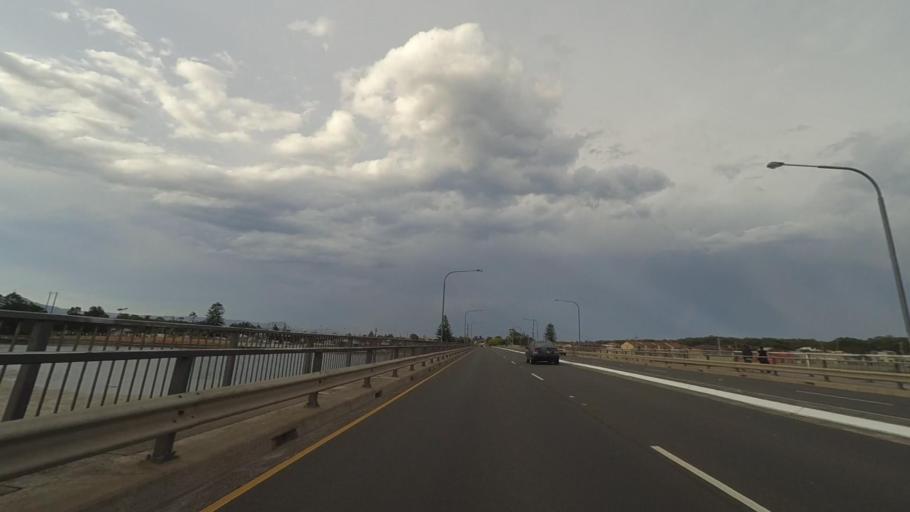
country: AU
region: New South Wales
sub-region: Shellharbour
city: Lake Illawarra
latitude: -34.5363
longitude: 150.8669
